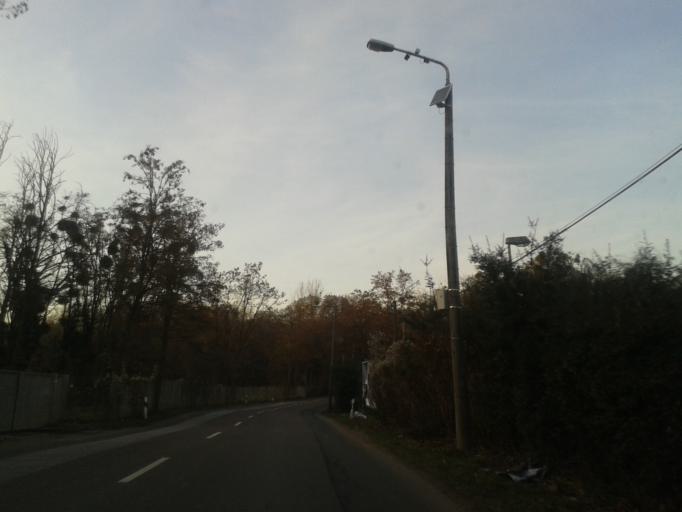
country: DE
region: Saxony
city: Albertstadt
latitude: 51.0901
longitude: 13.7413
